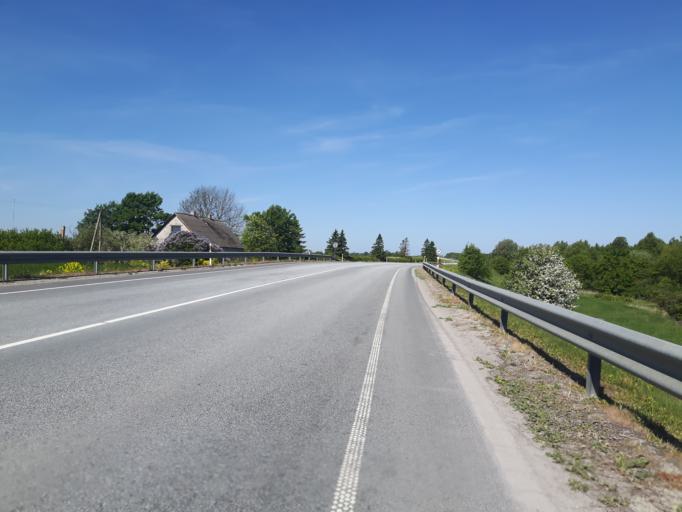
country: EE
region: Ida-Virumaa
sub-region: Kivioli linn
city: Kivioli
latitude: 59.4297
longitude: 26.9501
